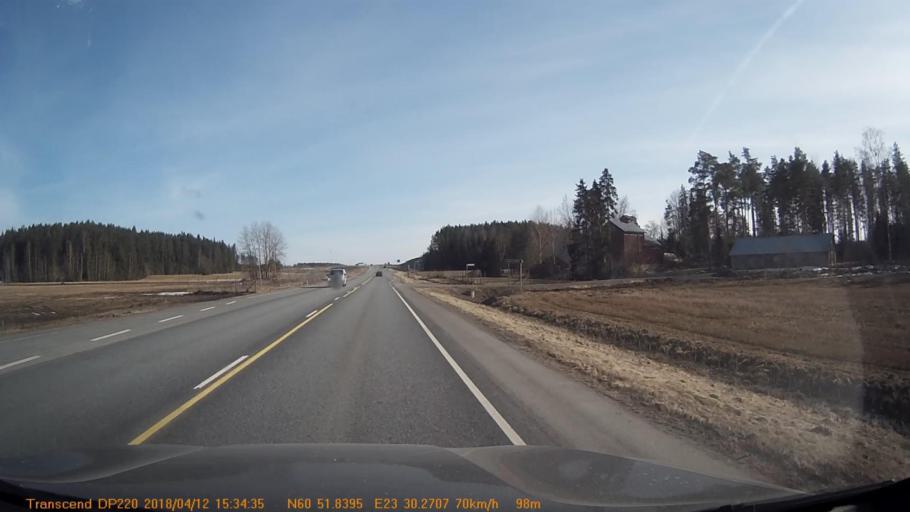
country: FI
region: Haeme
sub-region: Forssa
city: Jokioinen
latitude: 60.8638
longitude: 23.5048
